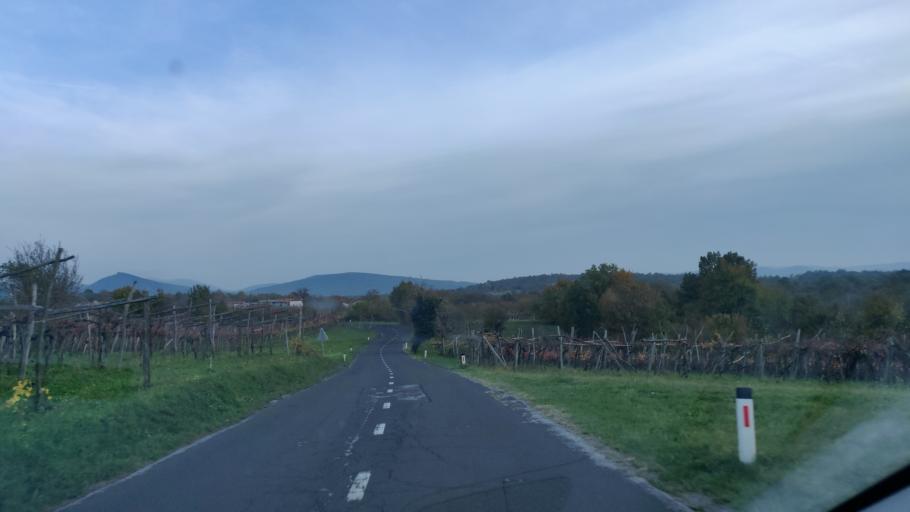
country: SI
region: Sezana
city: Sezana
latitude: 45.7642
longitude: 13.9004
